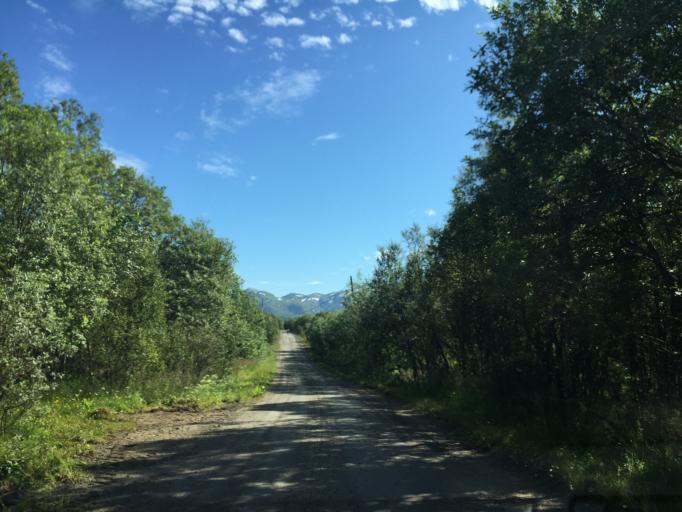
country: NO
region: Nordland
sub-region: Vagan
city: Kabelvag
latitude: 68.3545
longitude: 14.4487
